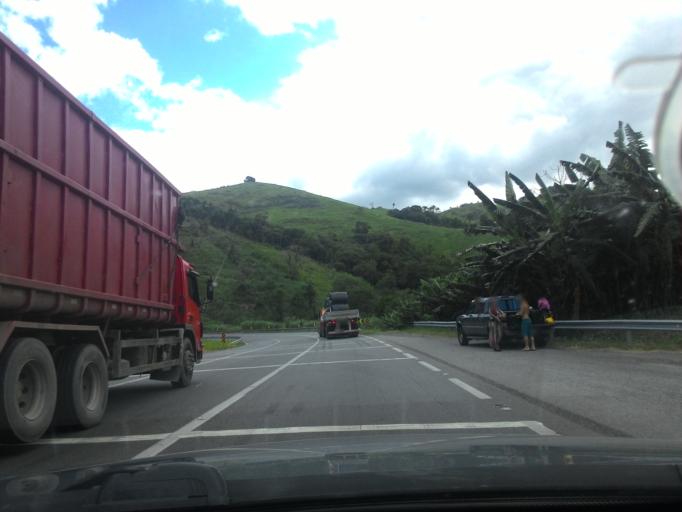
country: BR
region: Sao Paulo
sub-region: Cajati
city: Cajati
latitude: -24.7769
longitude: -48.2109
